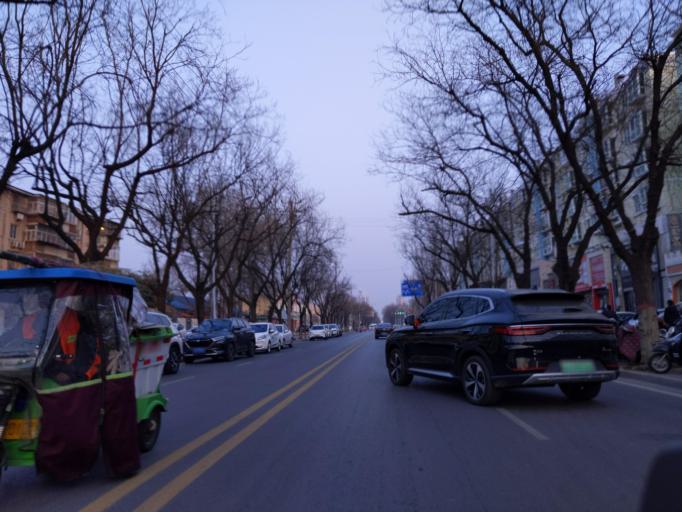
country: CN
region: Henan Sheng
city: Zhongyuanlu
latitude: 35.7702
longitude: 115.0888
